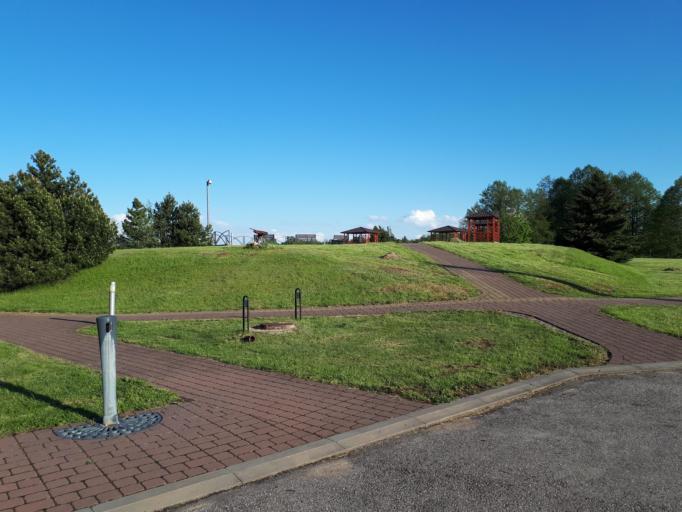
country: LT
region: Alytaus apskritis
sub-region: Alytaus rajonas
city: Daugai
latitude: 54.4672
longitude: 24.3850
